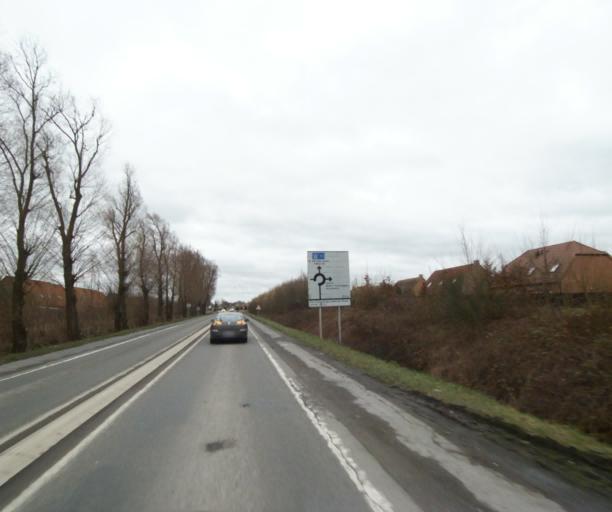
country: FR
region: Nord-Pas-de-Calais
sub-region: Departement du Nord
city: Saint-Saulve
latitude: 50.3823
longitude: 3.5582
